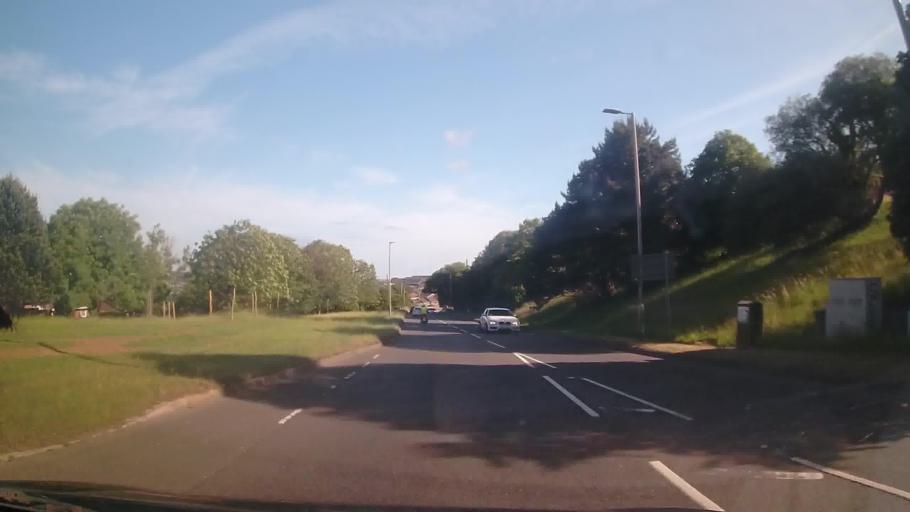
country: GB
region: England
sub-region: Devon
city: Plympton
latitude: 50.4100
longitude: -4.0945
